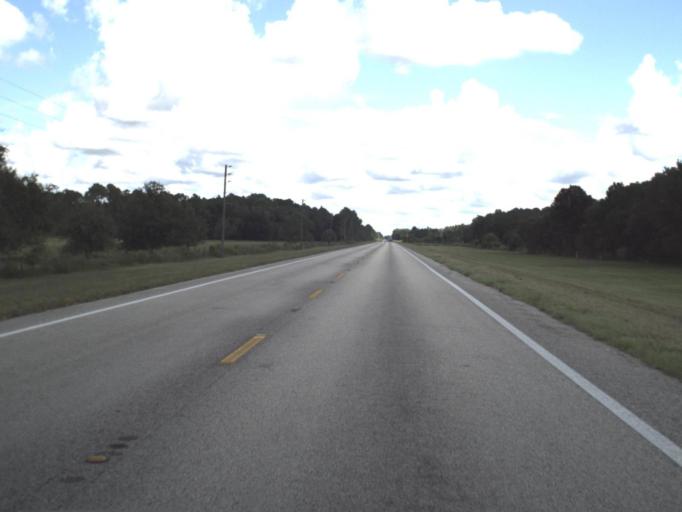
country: US
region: Florida
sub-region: Pasco County
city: Zephyrhills North
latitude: 28.2554
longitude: -82.0555
